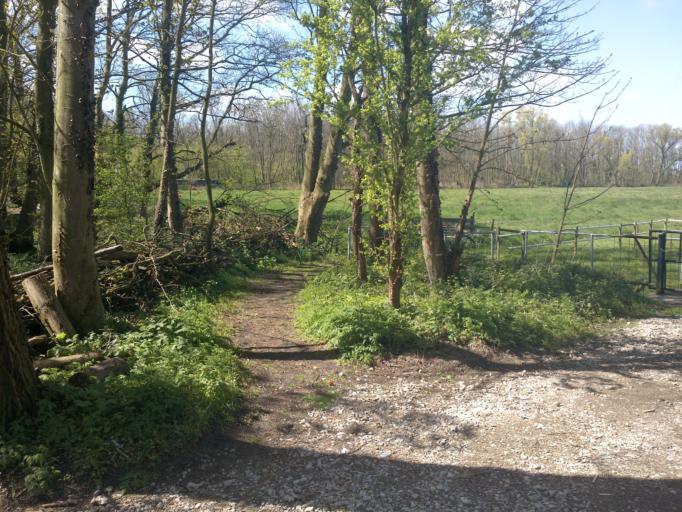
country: NL
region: South Holland
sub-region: Gemeente Lisse
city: Lisse
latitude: 52.2611
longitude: 4.5335
